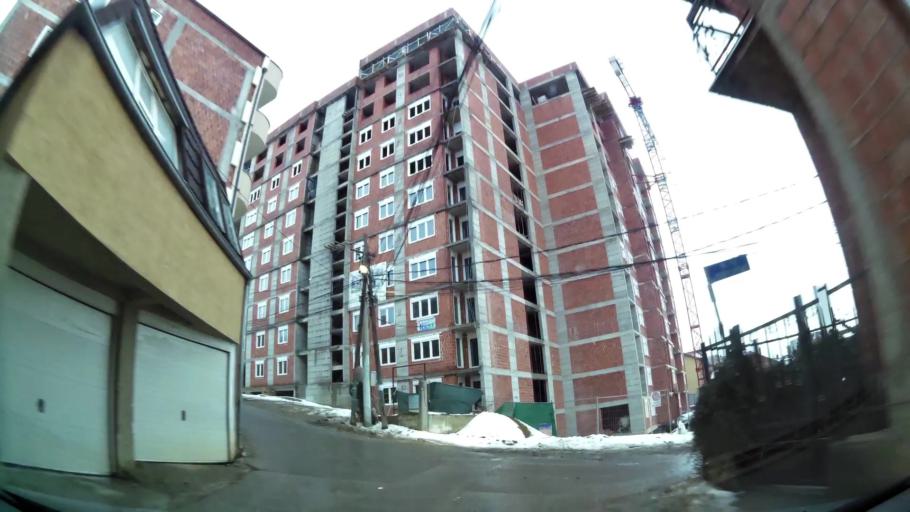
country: XK
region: Pristina
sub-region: Komuna e Prishtines
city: Pristina
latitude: 42.6577
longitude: 21.1725
